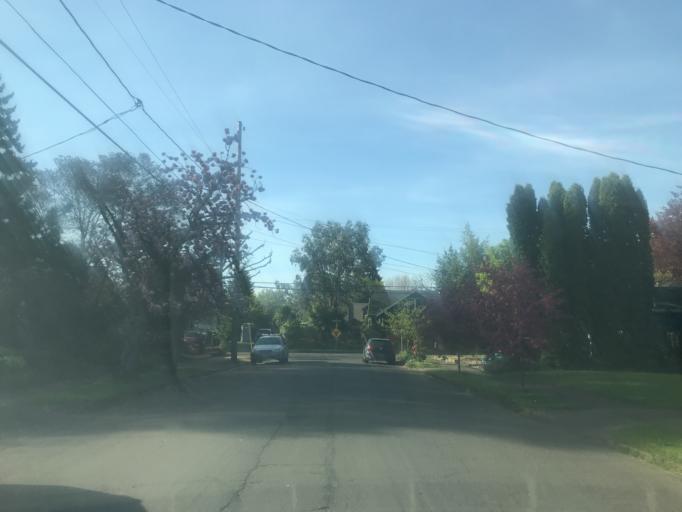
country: US
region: Oregon
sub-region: Multnomah County
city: Lents
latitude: 45.5020
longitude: -122.6012
